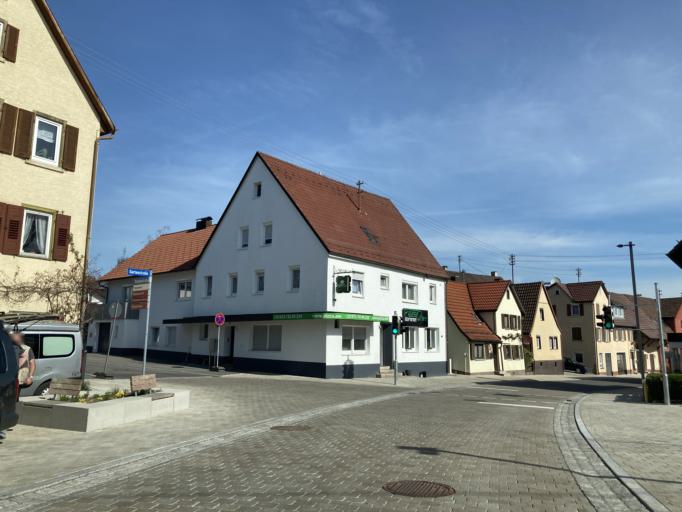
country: DE
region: Baden-Wuerttemberg
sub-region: Tuebingen Region
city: Nehren
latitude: 48.4291
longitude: 9.0675
